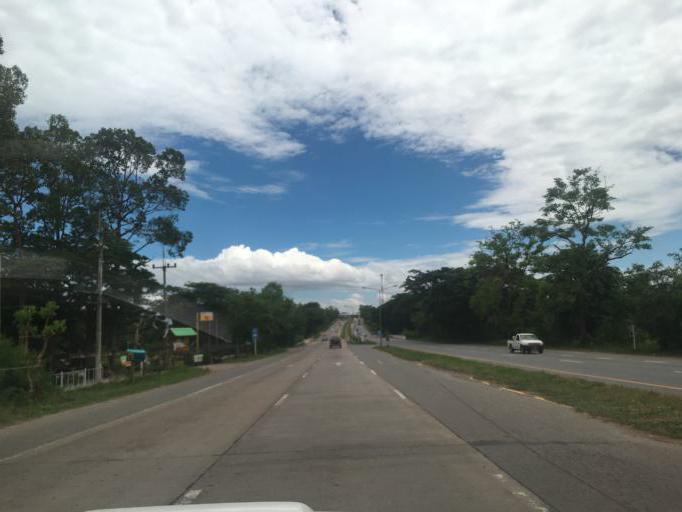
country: TH
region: Khon Kaen
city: Nam Phong
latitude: 16.6661
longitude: 102.8038
